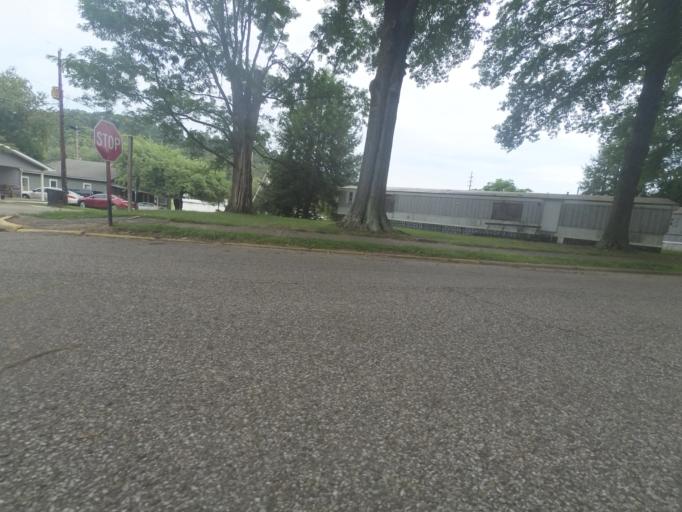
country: US
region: West Virginia
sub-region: Cabell County
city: Huntington
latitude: 38.4260
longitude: -82.4616
